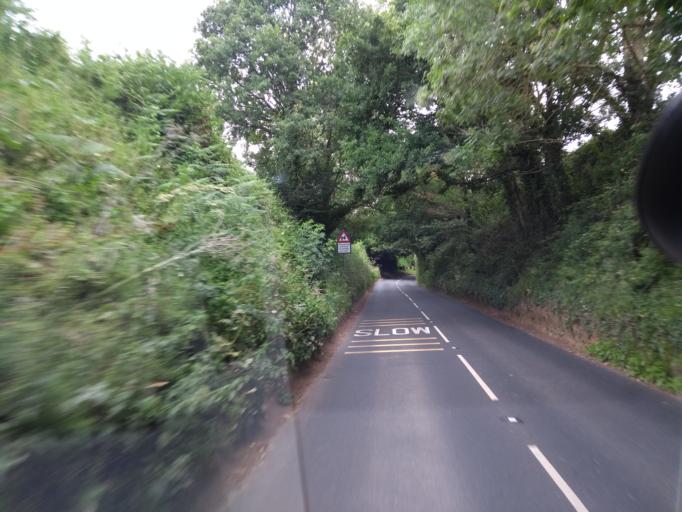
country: GB
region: England
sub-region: Somerset
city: South Petherton
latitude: 50.9281
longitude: -2.8206
